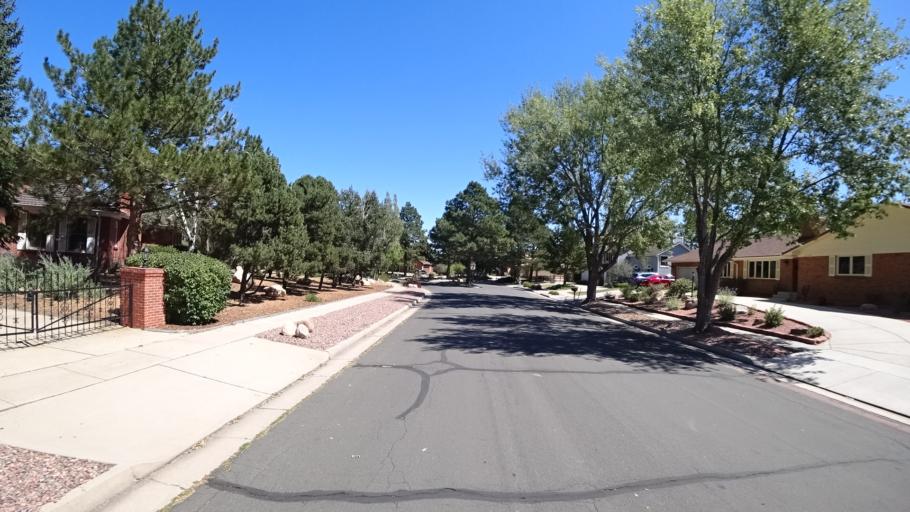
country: US
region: Colorado
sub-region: El Paso County
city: Colorado Springs
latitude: 38.7867
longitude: -104.8286
